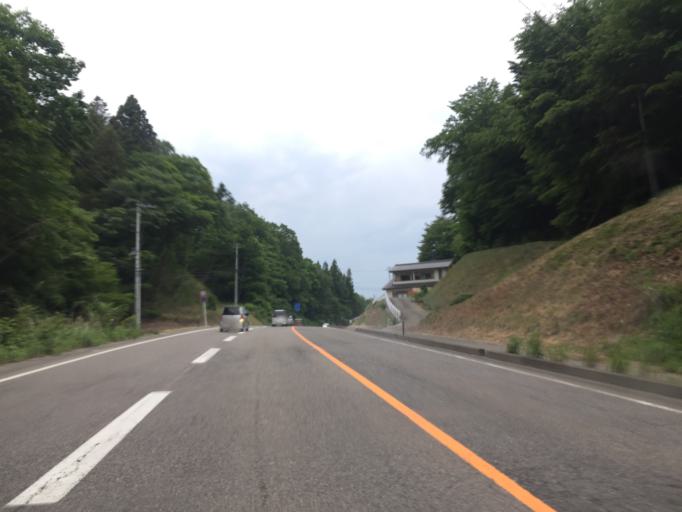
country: JP
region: Fukushima
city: Namie
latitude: 37.4323
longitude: 140.8042
